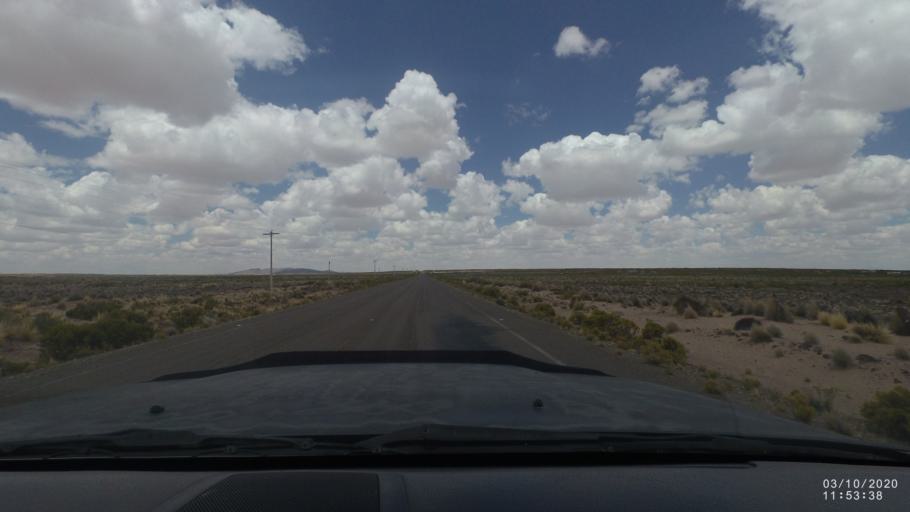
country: BO
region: Oruro
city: Poopo
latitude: -18.4822
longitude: -67.6051
